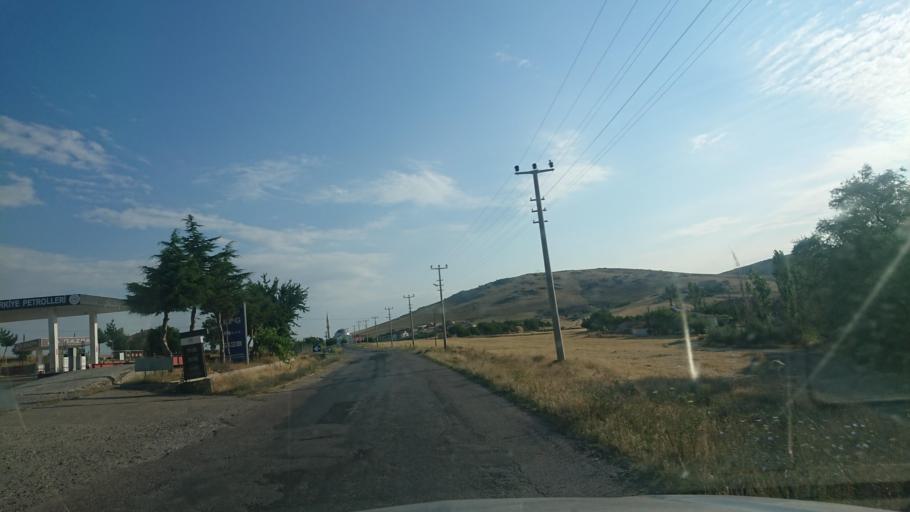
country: TR
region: Aksaray
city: Ortakoy
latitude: 38.7660
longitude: 34.0618
